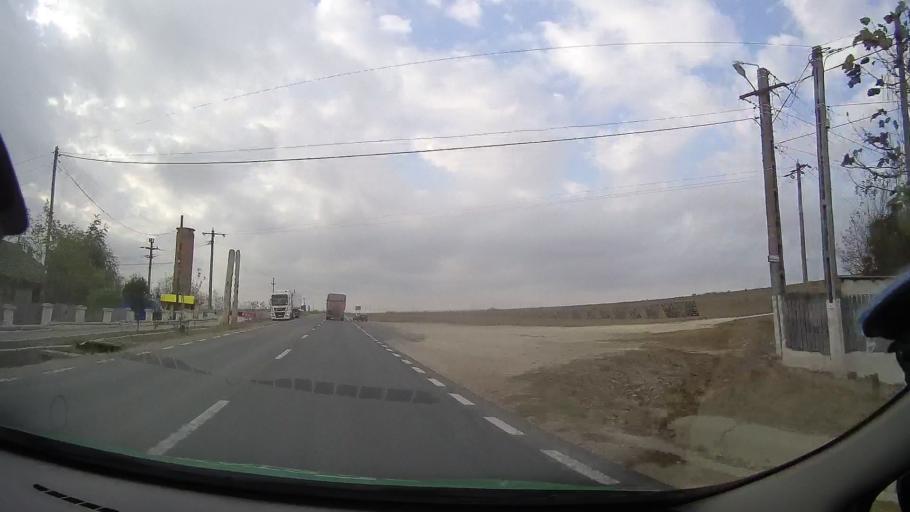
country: RO
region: Constanta
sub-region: Comuna Mircea Voda
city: Satu Nou
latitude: 44.2692
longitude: 28.2178
